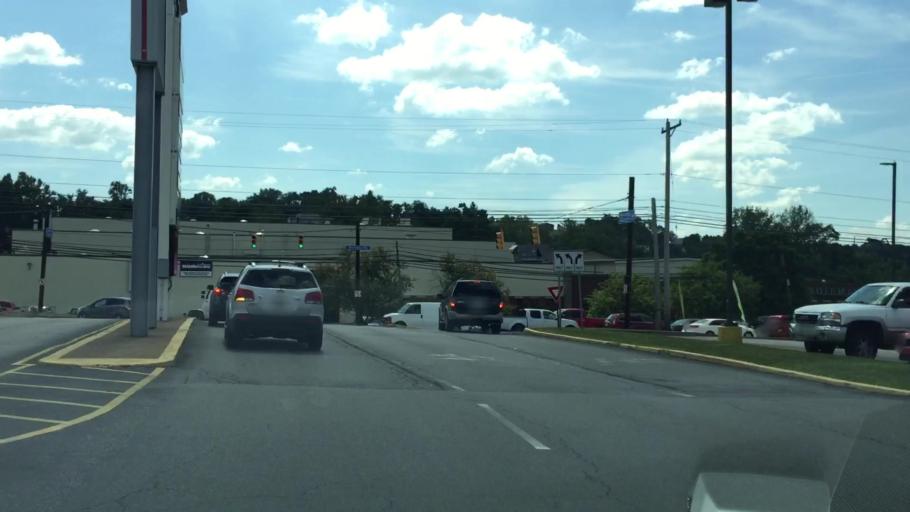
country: US
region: Pennsylvania
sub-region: Allegheny County
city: Bridgeville
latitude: 40.3659
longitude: -80.1088
